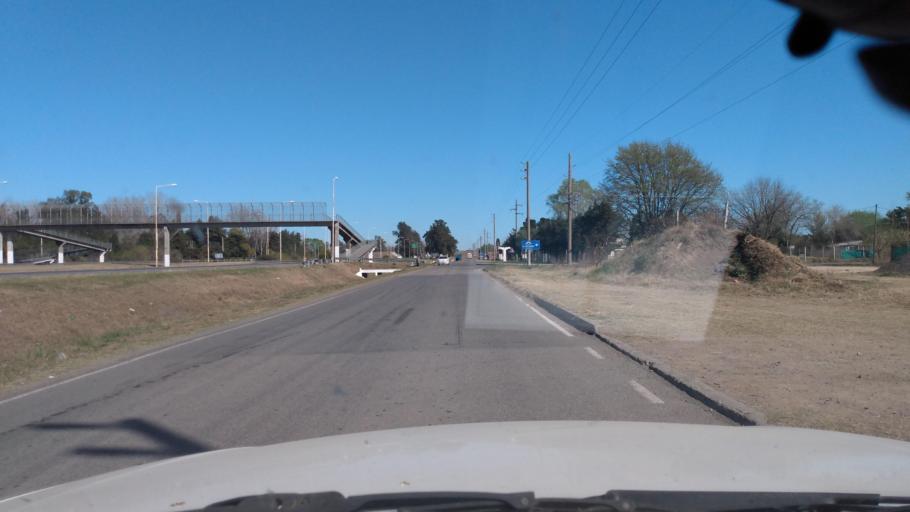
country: AR
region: Buenos Aires
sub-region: Partido de Mercedes
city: Mercedes
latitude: -34.6544
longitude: -59.3466
